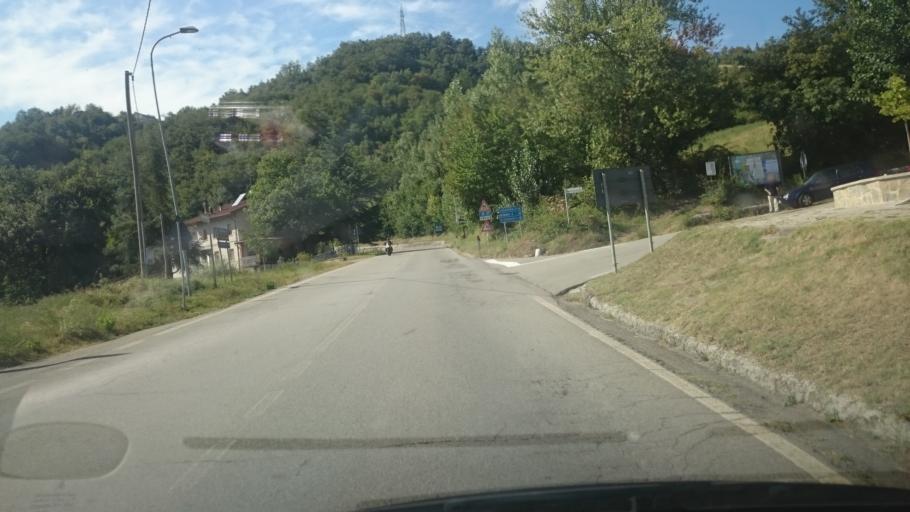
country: IT
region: Emilia-Romagna
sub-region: Provincia di Modena
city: Montefiorino
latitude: 44.4076
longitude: 10.6150
